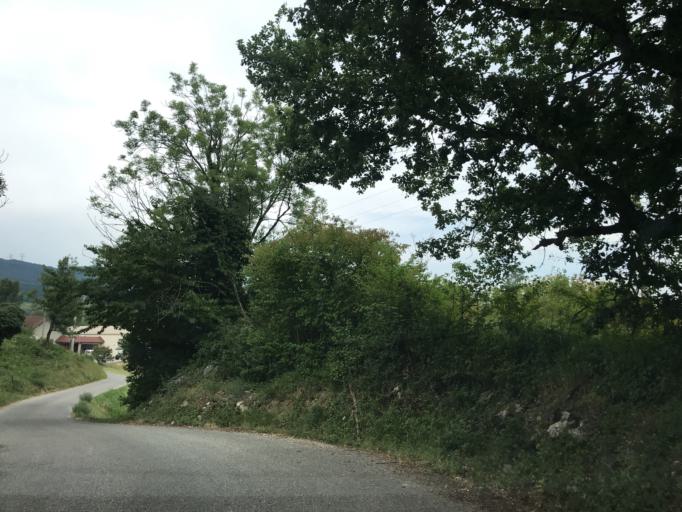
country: FR
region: Rhone-Alpes
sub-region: Departement de la Savoie
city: Les Marches
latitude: 45.4952
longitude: 5.9673
